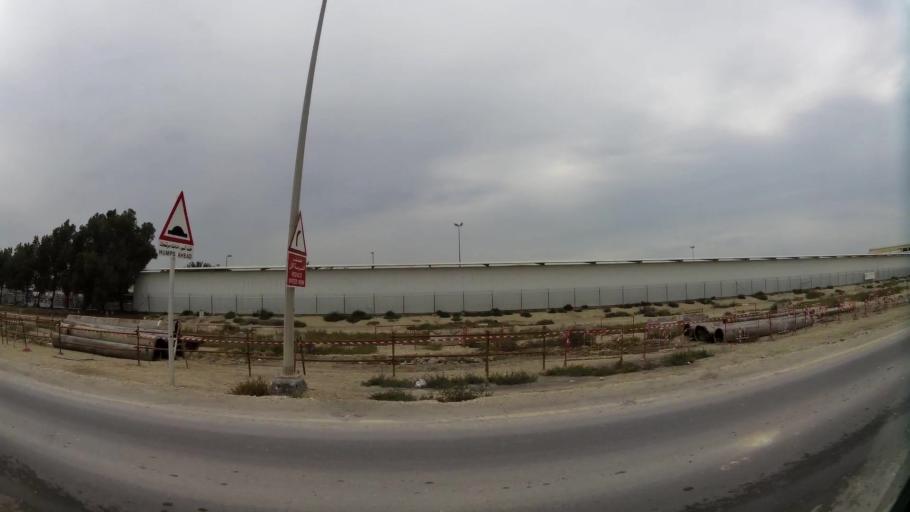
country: BH
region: Northern
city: Sitrah
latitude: 26.1782
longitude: 50.6208
